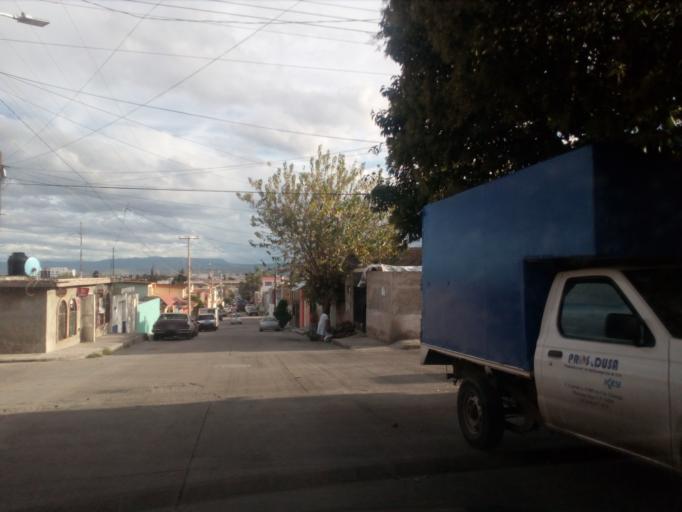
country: MX
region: Durango
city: Victoria de Durango
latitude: 24.0436
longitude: -104.6658
